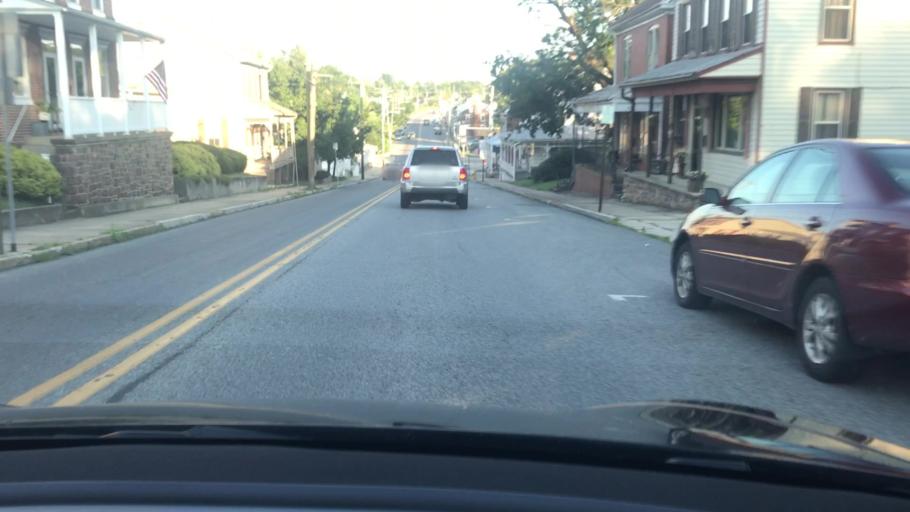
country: US
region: Pennsylvania
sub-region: York County
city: Dover
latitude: 40.0003
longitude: -76.8491
